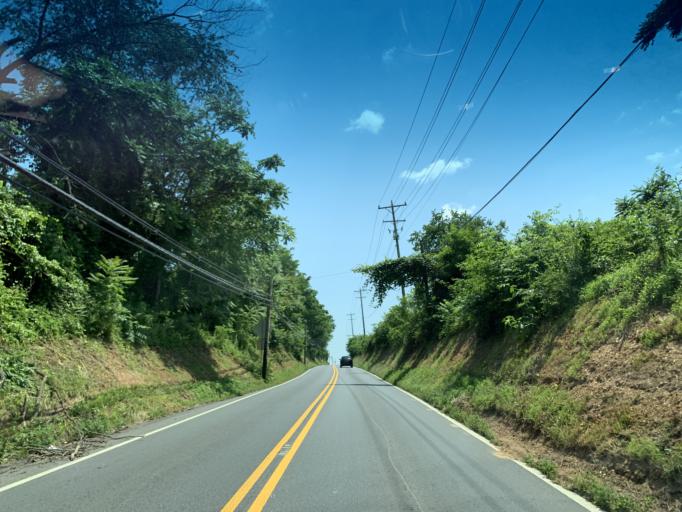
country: US
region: Maryland
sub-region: Frederick County
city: Green Valley
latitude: 39.3681
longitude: -77.2716
